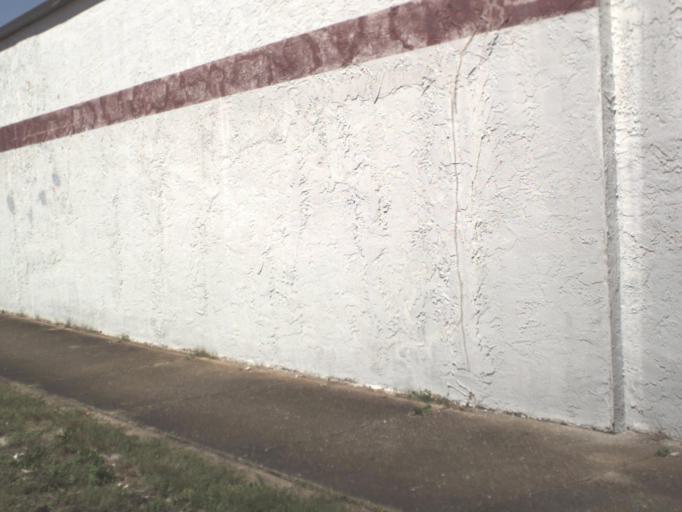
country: US
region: Florida
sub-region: Escambia County
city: Pensacola
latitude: 30.4281
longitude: -87.2188
